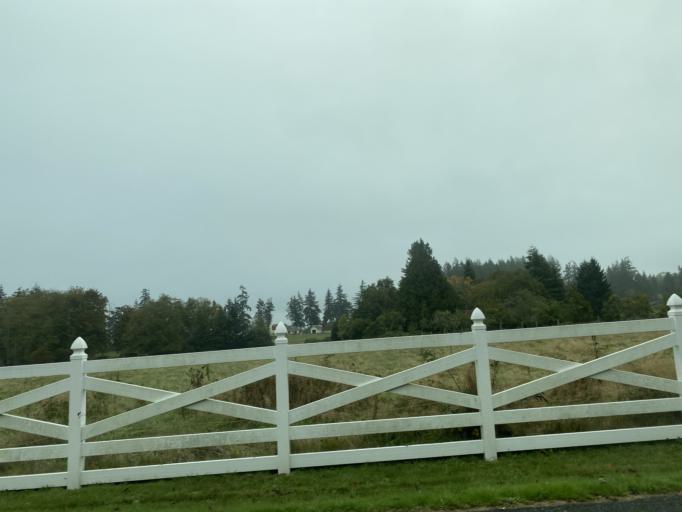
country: US
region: Washington
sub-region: Island County
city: Freeland
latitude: 48.0824
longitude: -122.4850
